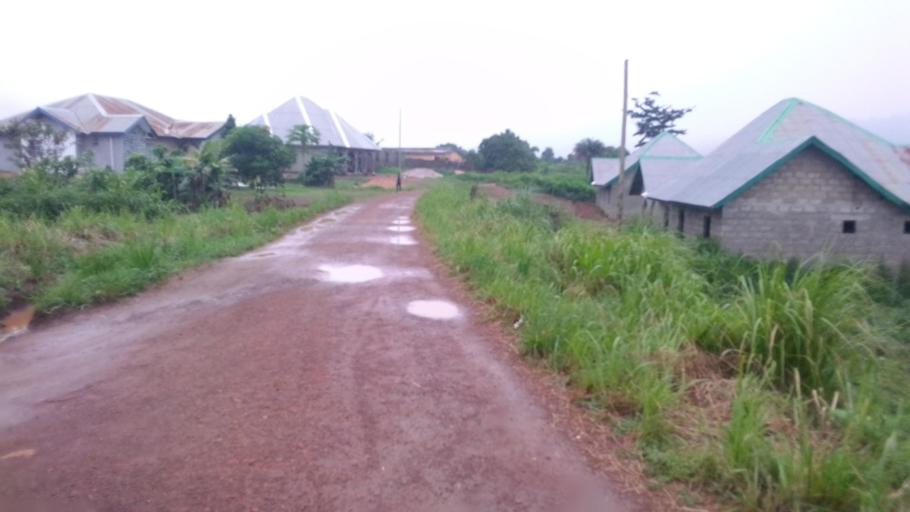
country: SL
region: Eastern Province
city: Kenema
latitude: 7.9017
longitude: -11.1609
